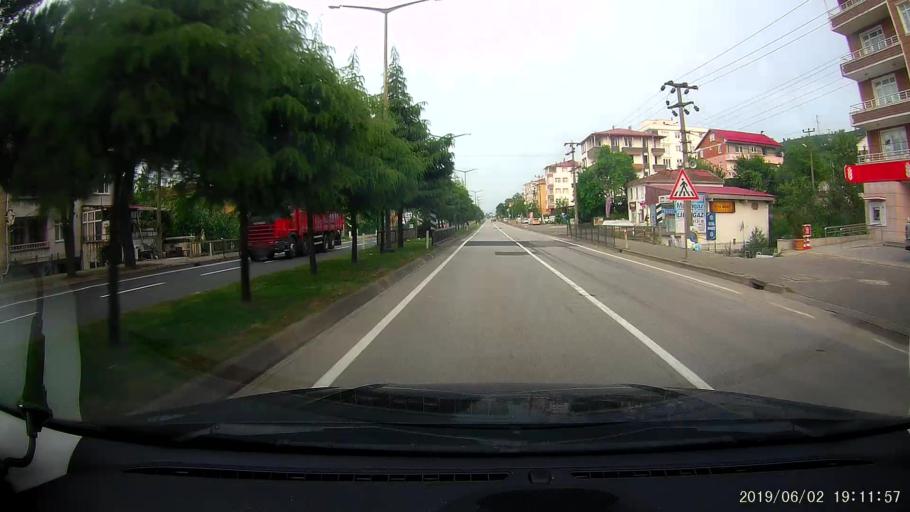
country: TR
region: Ordu
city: Gulyali
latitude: 40.9665
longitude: 38.0607
